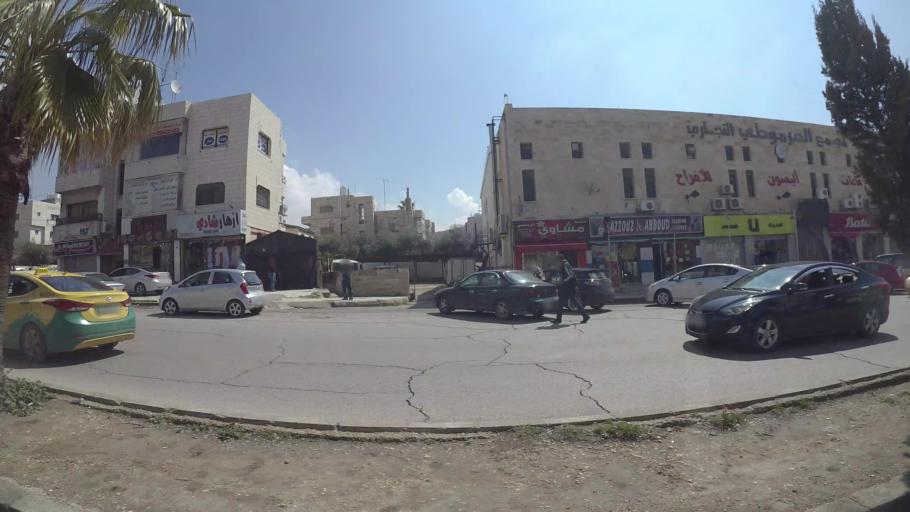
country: JO
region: Amman
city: Al Bunayyat ash Shamaliyah
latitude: 31.9304
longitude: 35.9102
